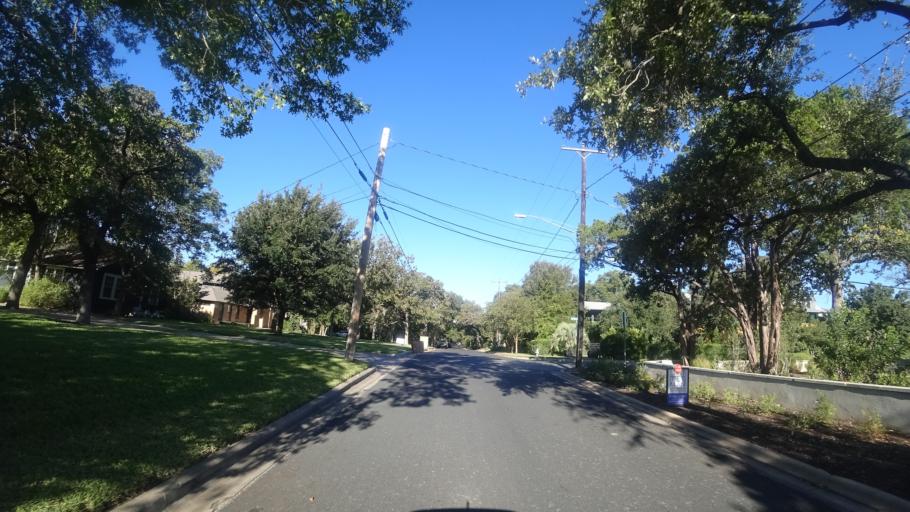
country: US
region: Texas
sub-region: Travis County
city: Rollingwood
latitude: 30.2851
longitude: -97.7674
